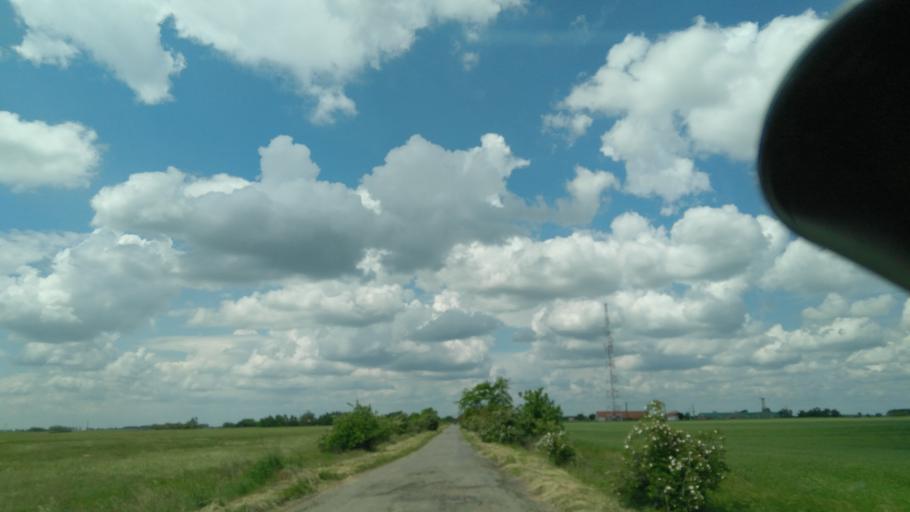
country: HU
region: Bekes
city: Devavanya
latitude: 47.0228
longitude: 20.9345
